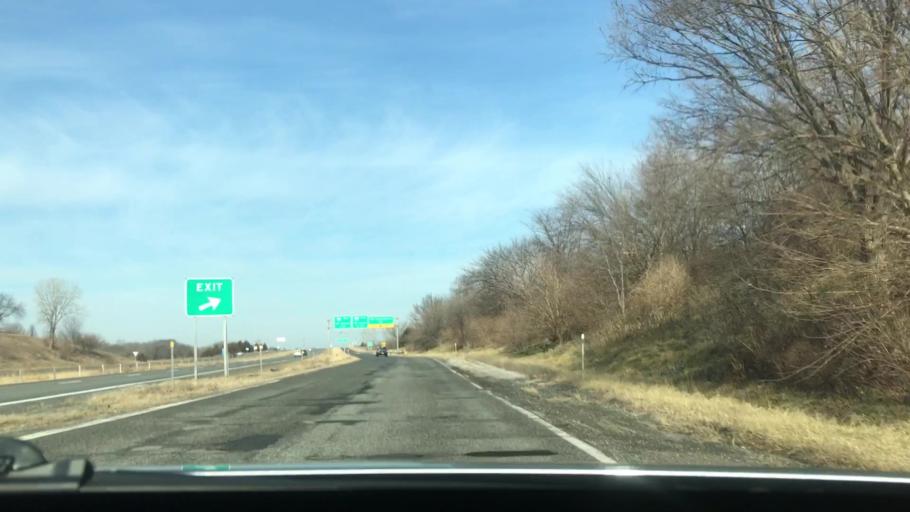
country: US
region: Missouri
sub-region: Clay County
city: Smithville
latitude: 39.2972
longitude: -94.5847
